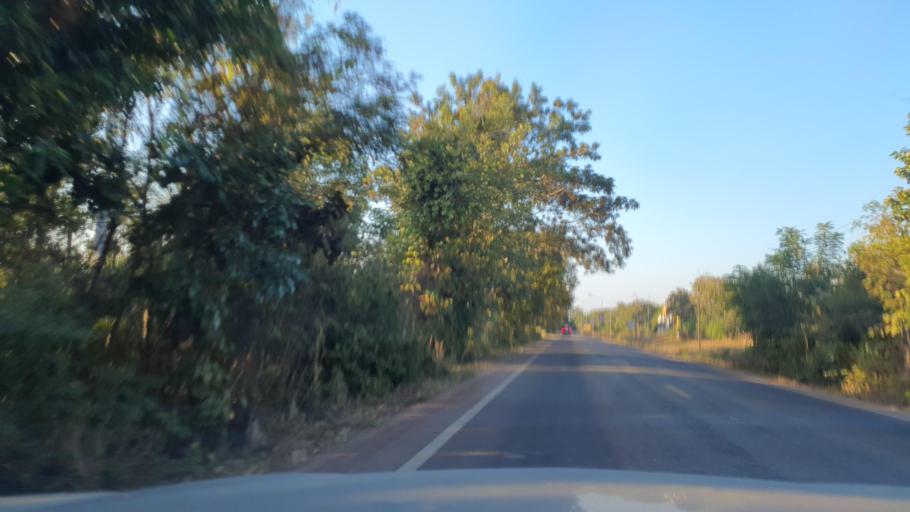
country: TH
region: Nakhon Phanom
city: Si Songkhram
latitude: 17.5582
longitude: 104.2381
